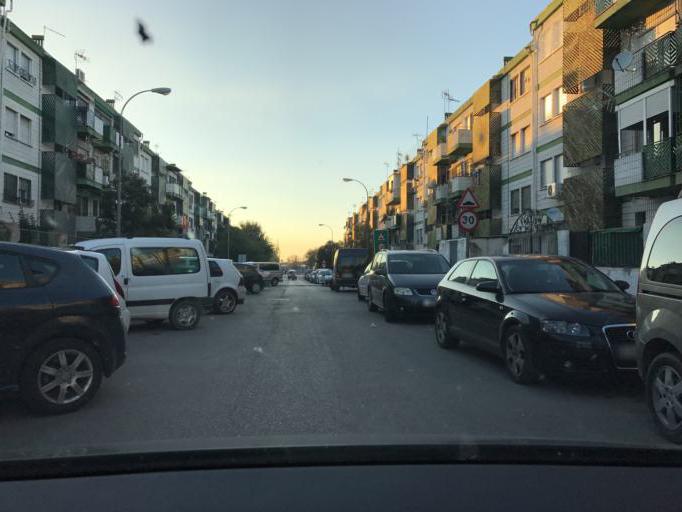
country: ES
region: Andalusia
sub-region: Provincia de Granada
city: Pulianas
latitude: 37.2088
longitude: -3.6063
